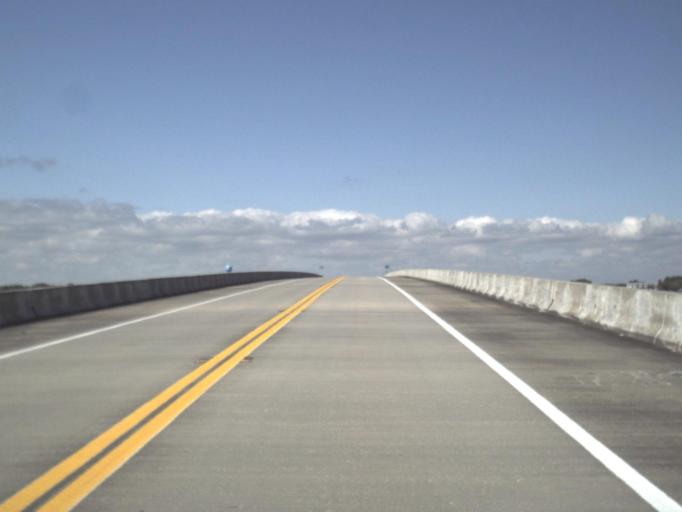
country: US
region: Florida
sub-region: Wakulla County
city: Crawfordville
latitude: 29.9667
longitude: -84.3841
